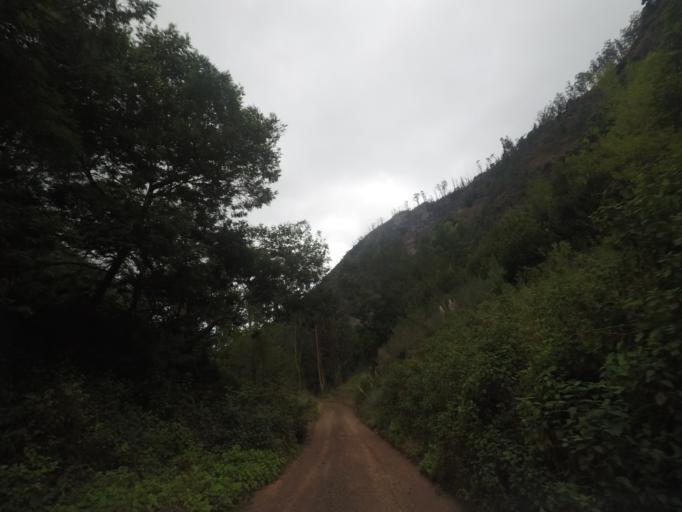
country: PT
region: Madeira
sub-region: Funchal
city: Nossa Senhora do Monte
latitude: 32.6924
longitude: -16.9175
